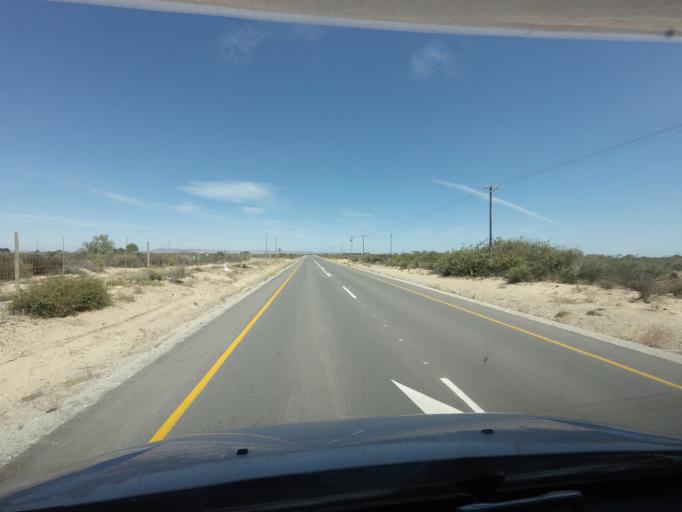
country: ZA
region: Western Cape
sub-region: West Coast District Municipality
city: Vredenburg
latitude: -32.7939
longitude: 18.2359
